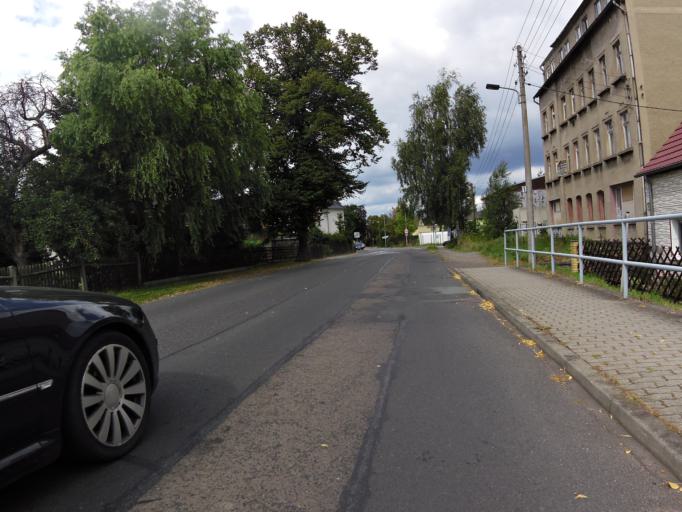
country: DE
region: Saxony
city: Rackwitz
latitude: 51.3934
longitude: 12.3399
